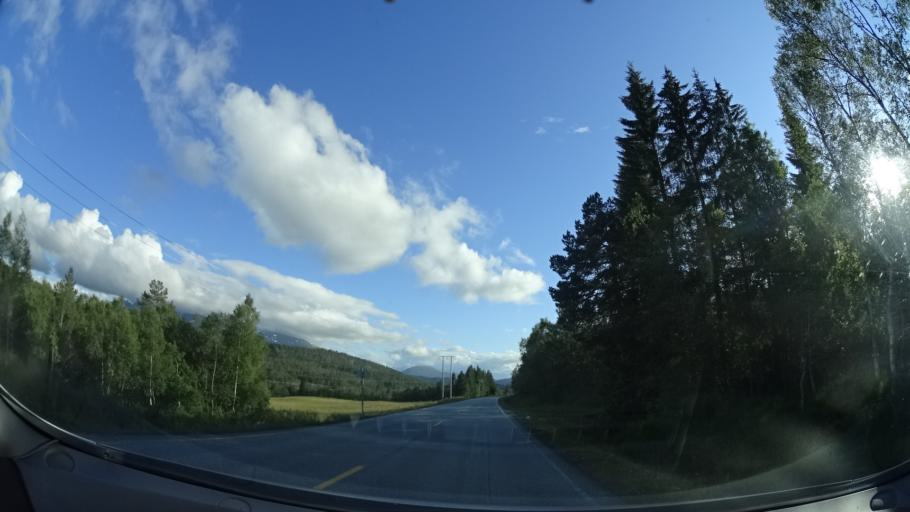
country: NO
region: More og Romsdal
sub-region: Molde
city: Hjelset
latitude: 62.8143
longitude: 7.5943
